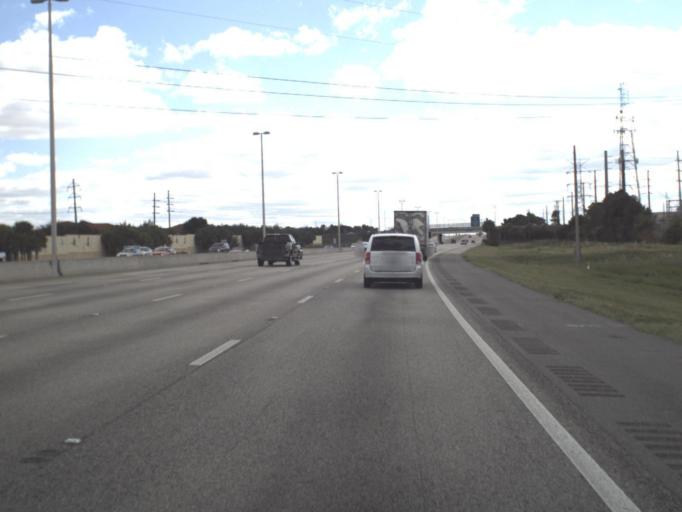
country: US
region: Florida
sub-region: Orange County
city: Tangelo Park
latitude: 28.4866
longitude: -81.4554
